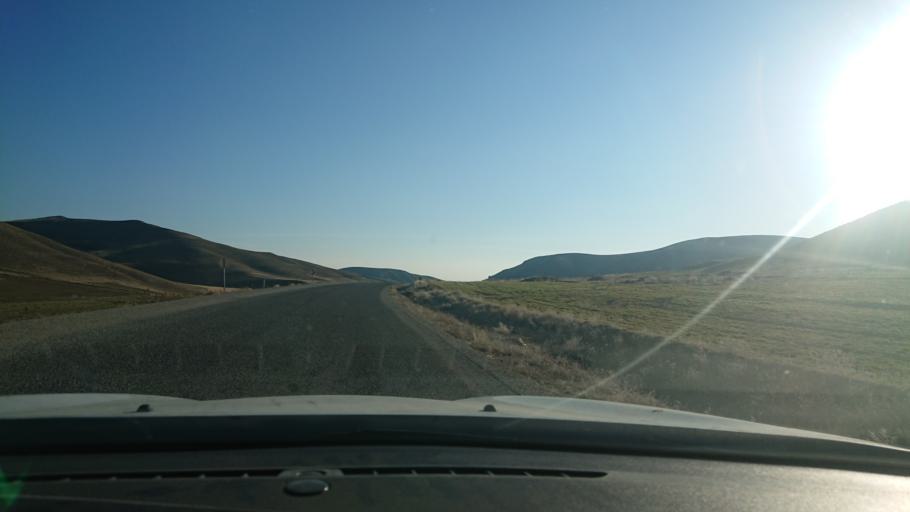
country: TR
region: Aksaray
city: Acipinar
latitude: 38.7031
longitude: 33.7546
